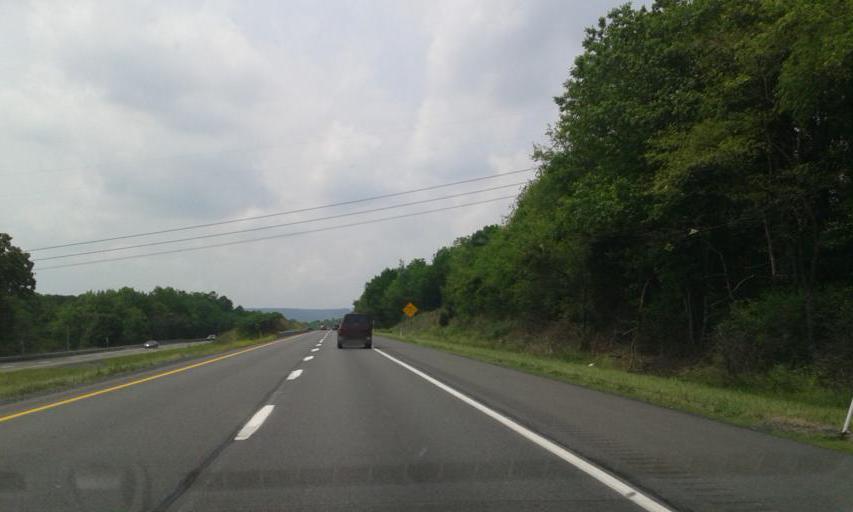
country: US
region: Pennsylvania
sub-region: Northampton County
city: Belfast
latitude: 40.7971
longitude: -75.2924
